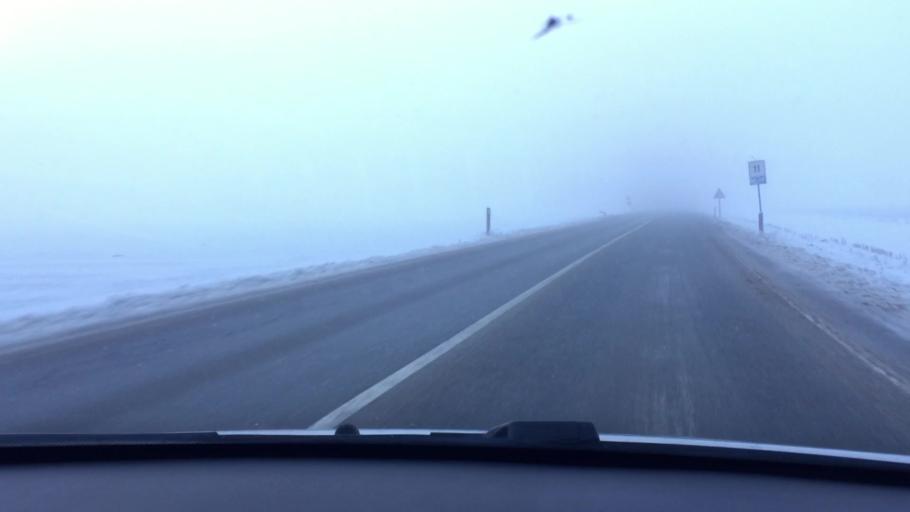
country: IT
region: Piedmont
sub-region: Provincia di Torino
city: Scalenghe
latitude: 44.9045
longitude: 7.4912
